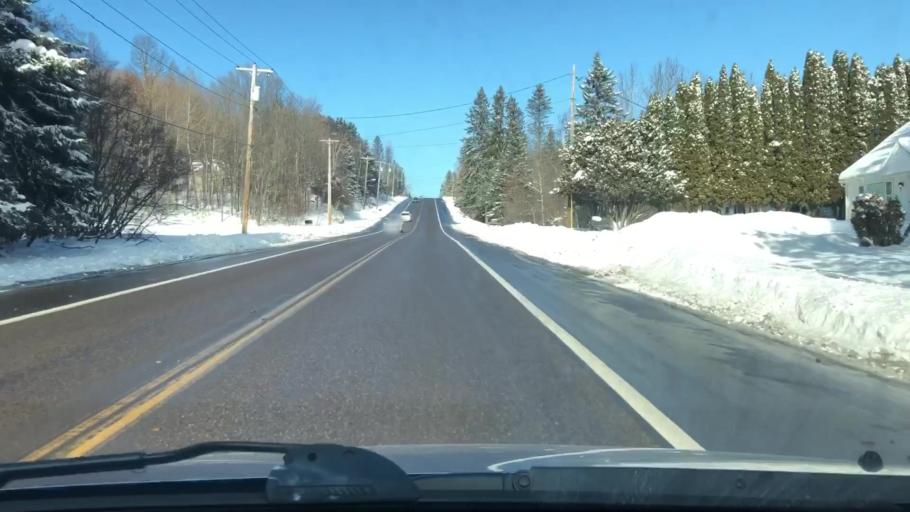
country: US
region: Minnesota
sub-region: Saint Louis County
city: Duluth
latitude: 46.8098
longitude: -92.1321
